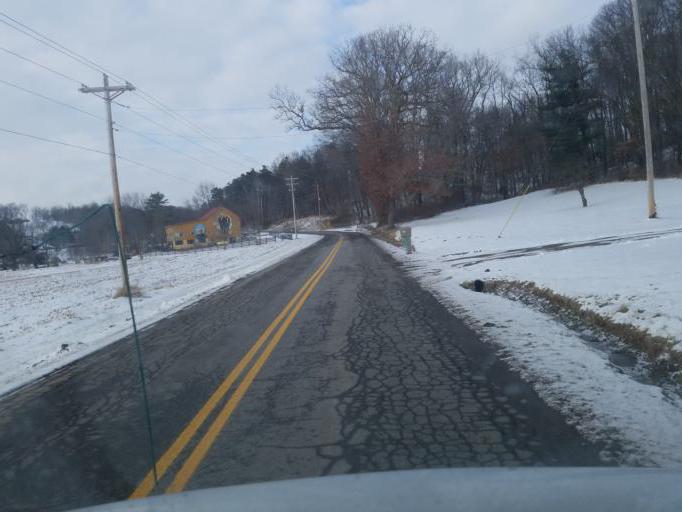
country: US
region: Ohio
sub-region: Holmes County
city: Millersburg
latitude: 40.4574
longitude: -81.9062
